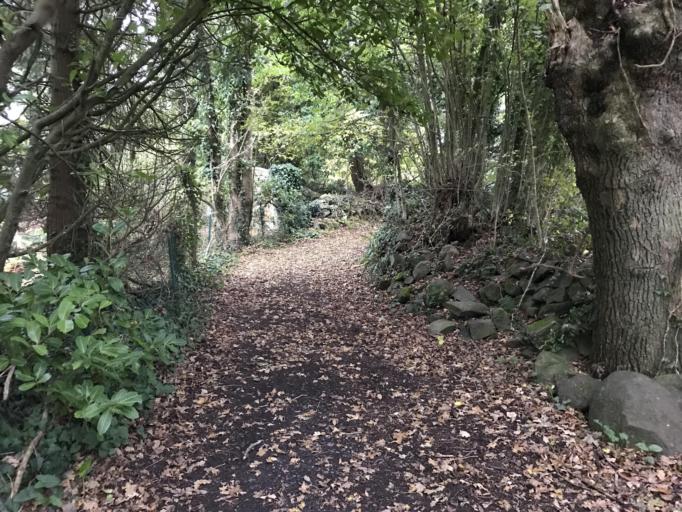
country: FR
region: Brittany
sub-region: Departement du Finistere
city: Logonna-Daoulas
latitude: 48.3350
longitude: -4.3067
